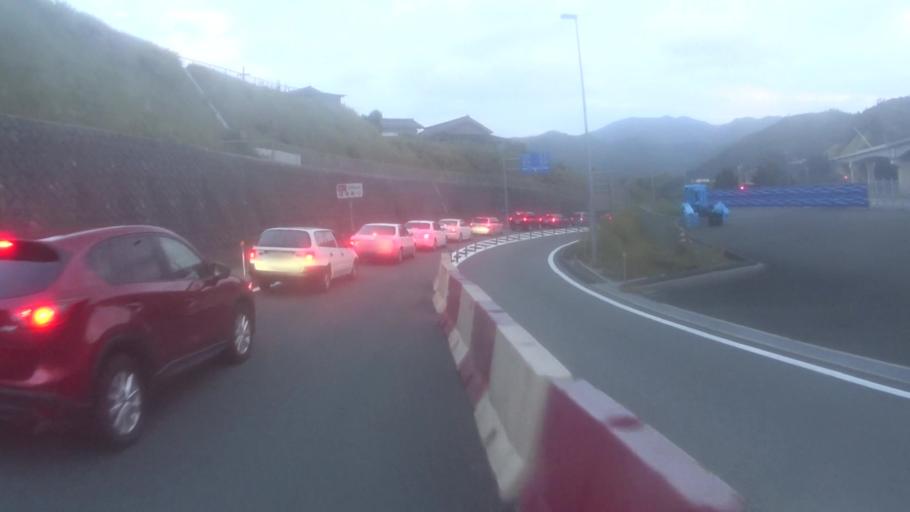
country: JP
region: Kyoto
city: Ayabe
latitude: 35.2771
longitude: 135.3392
